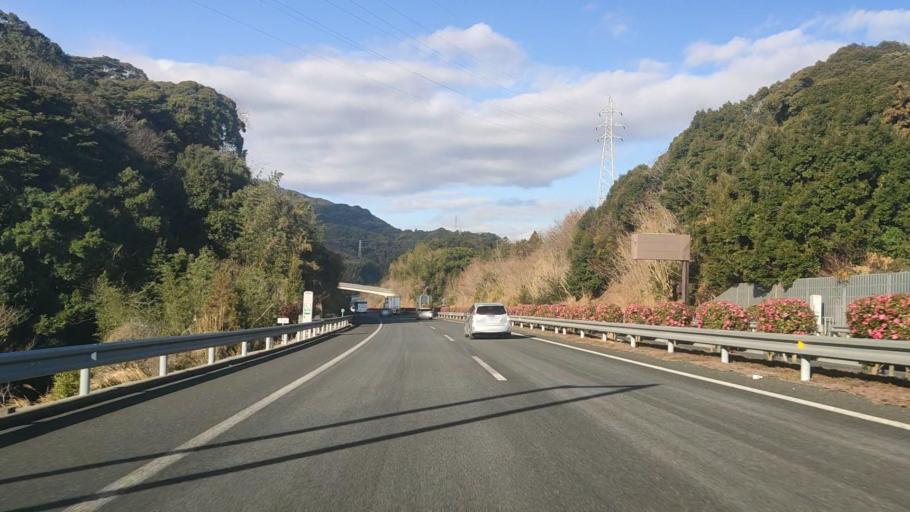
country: JP
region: Fukuoka
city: Kanda
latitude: 33.7984
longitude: 130.9600
